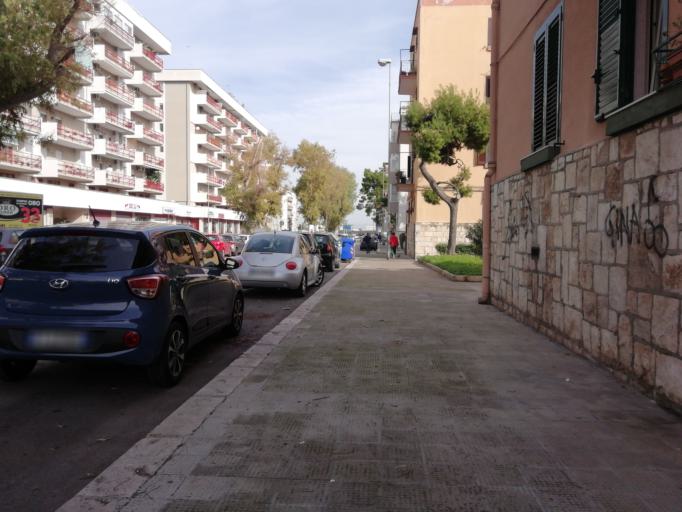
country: IT
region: Apulia
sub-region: Provincia di Bari
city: Bari
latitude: 41.1135
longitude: 16.8929
